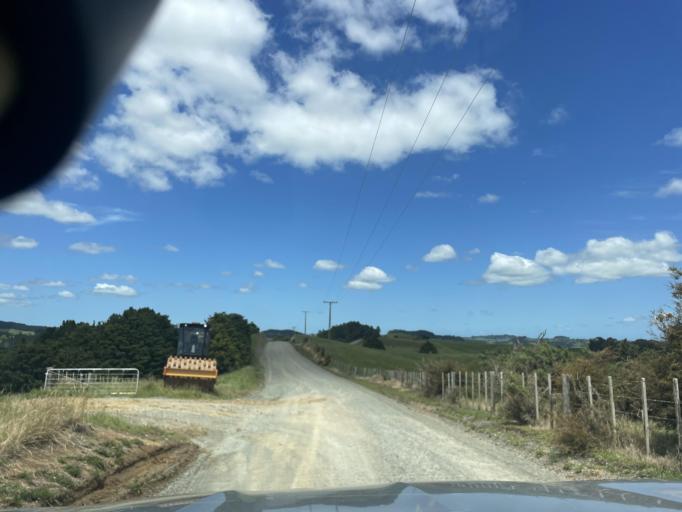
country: NZ
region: Auckland
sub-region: Auckland
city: Wellsford
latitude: -36.1578
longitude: 174.5389
